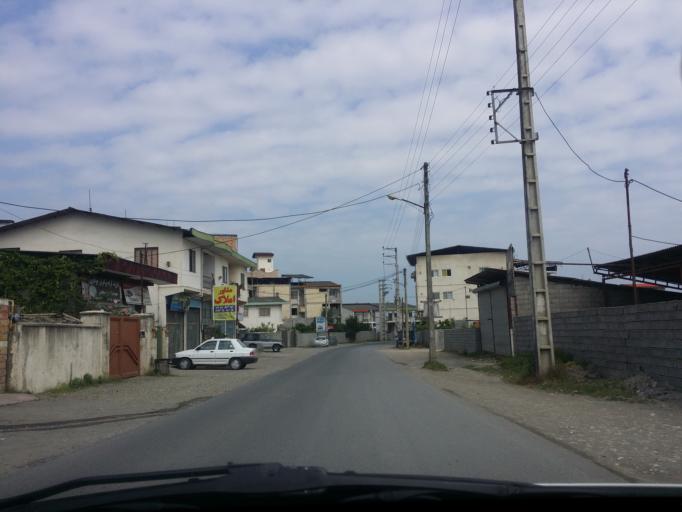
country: IR
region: Mazandaran
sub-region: Nowshahr
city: Nowshahr
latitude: 36.6275
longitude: 51.4851
